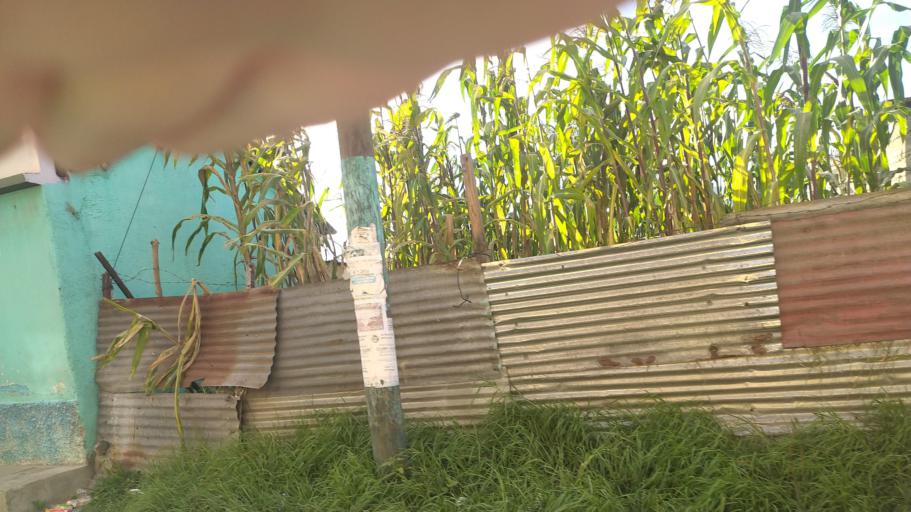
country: GT
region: Quetzaltenango
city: Salcaja
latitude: 14.8760
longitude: -91.4559
